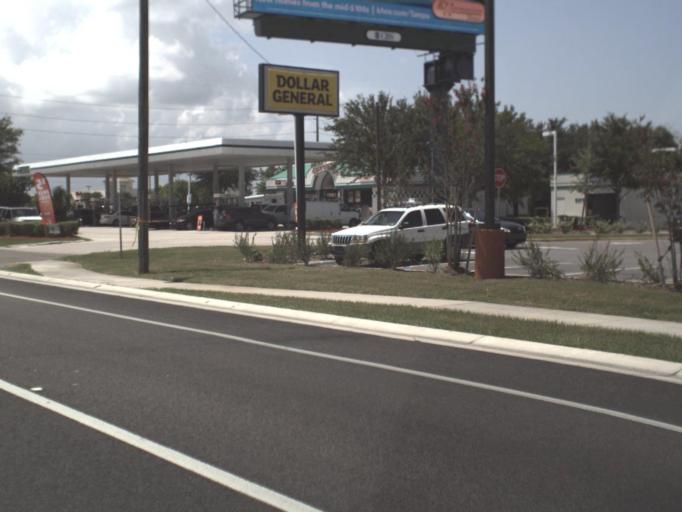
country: US
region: Florida
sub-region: Hillsborough County
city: Riverview
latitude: 27.7934
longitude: -82.3350
